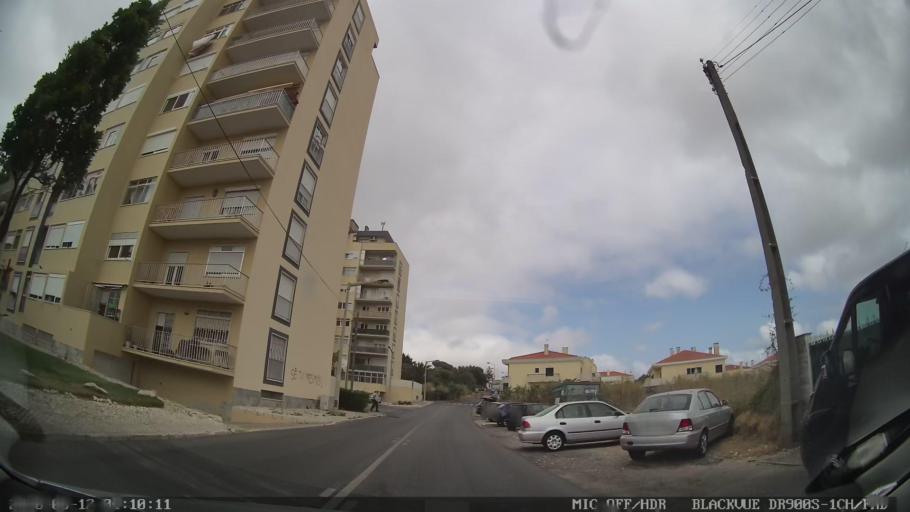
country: PT
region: Lisbon
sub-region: Cascais
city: Estoril
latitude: 38.7043
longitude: -9.3788
